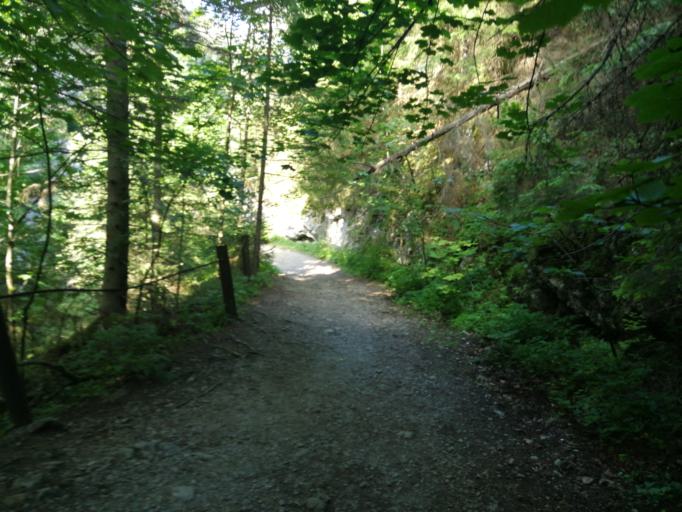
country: SK
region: Zilinsky
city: Tvrdosin
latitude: 49.1964
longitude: 19.5361
